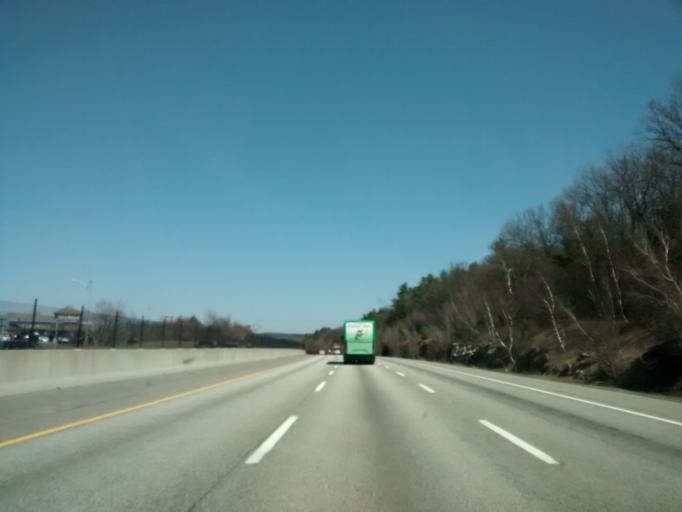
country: US
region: Massachusetts
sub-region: Worcester County
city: Westborough
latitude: 42.2432
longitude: -71.5929
